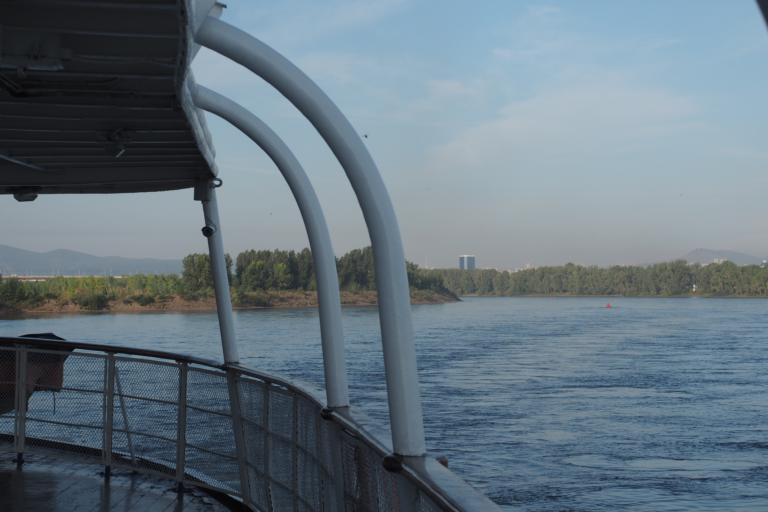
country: RU
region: Krasnoyarskiy
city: Solnechnyy
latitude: 56.0313
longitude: 92.9789
